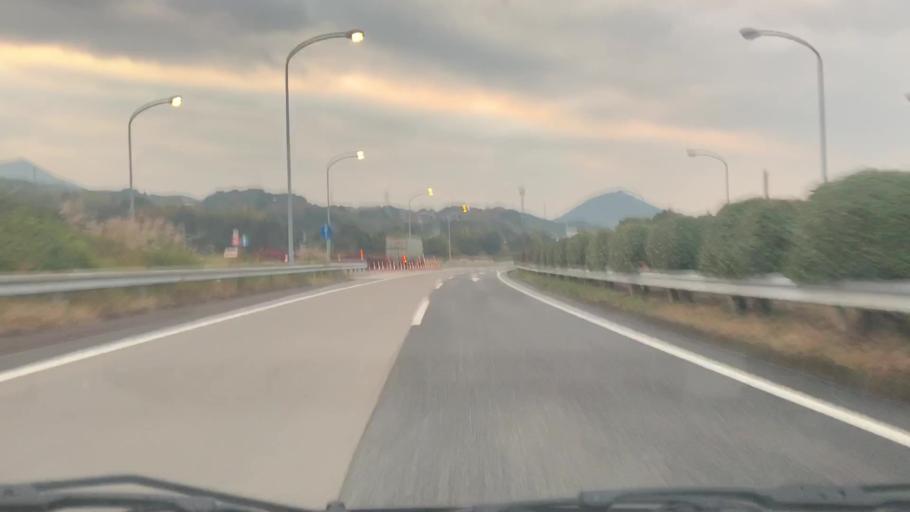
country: JP
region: Nagasaki
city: Omura
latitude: 33.0164
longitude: 129.9489
